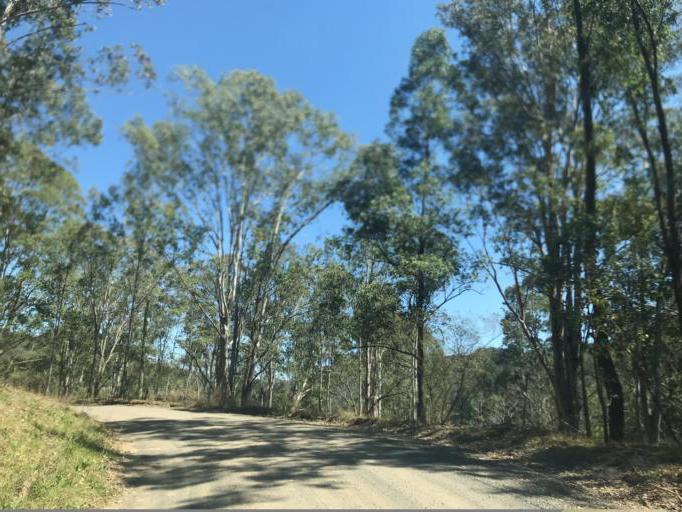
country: AU
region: New South Wales
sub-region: Hornsby Shire
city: Glenorie
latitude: -33.2593
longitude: 150.9728
